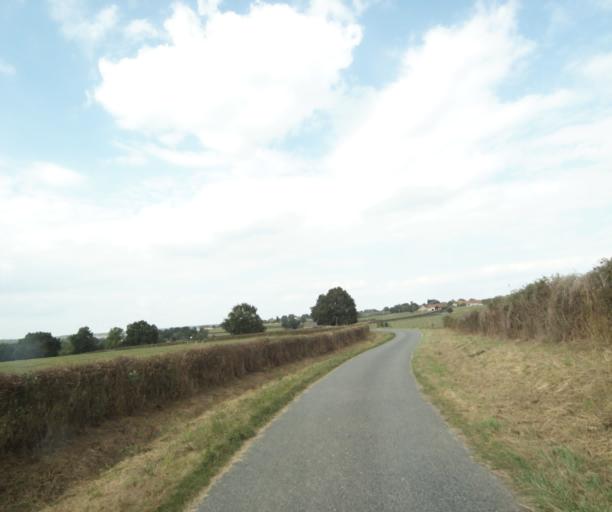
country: FR
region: Bourgogne
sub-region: Departement de Saone-et-Loire
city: Palinges
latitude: 46.4860
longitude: 4.1952
